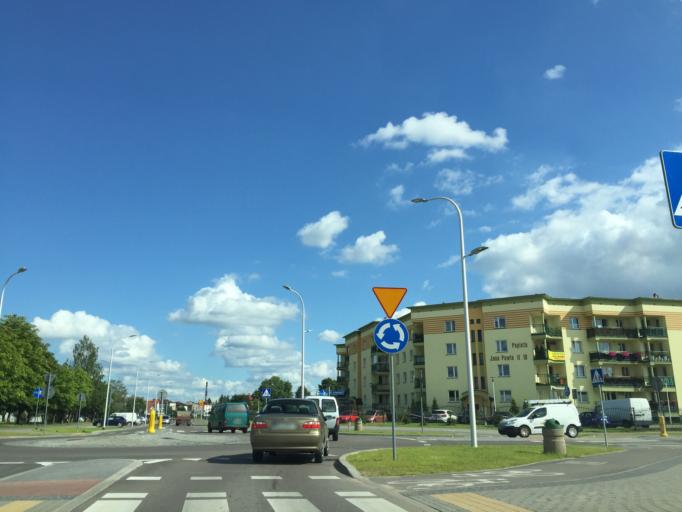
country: PL
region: Podlasie
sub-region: Suwalki
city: Suwalki
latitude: 54.1146
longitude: 22.9398
